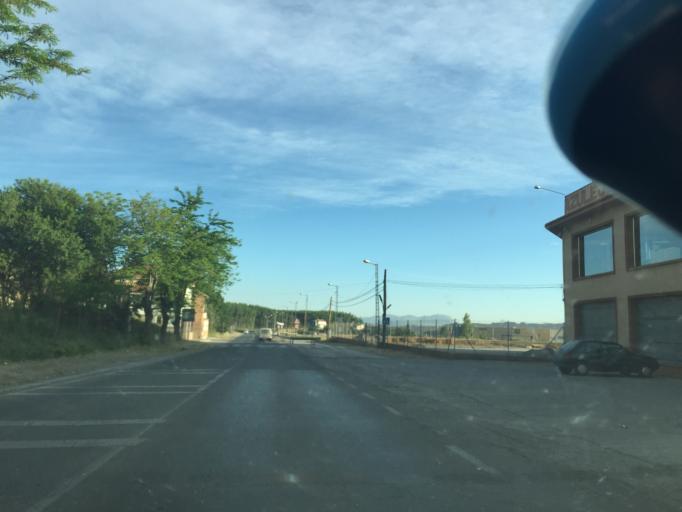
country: ES
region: Andalusia
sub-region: Provincia de Granada
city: Guadix
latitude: 37.3075
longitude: -3.1455
